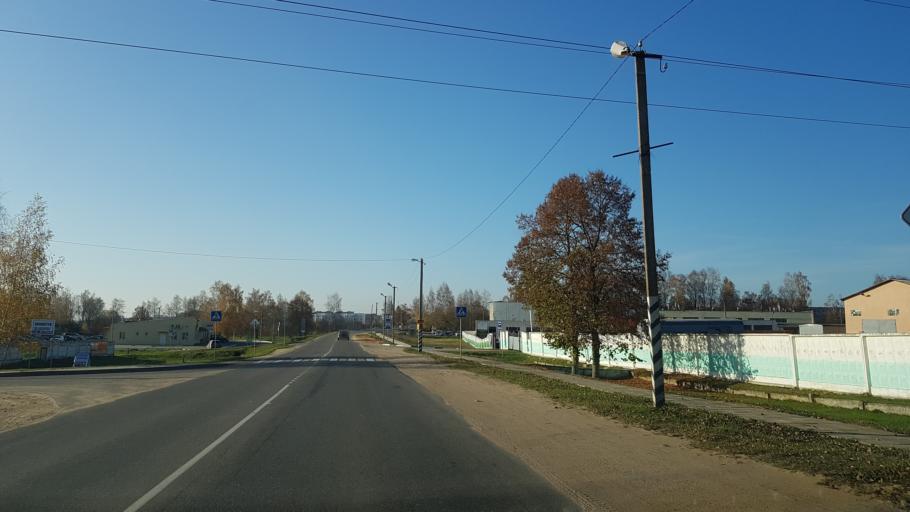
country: BY
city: Fanipol
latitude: 53.7363
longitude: 27.3246
